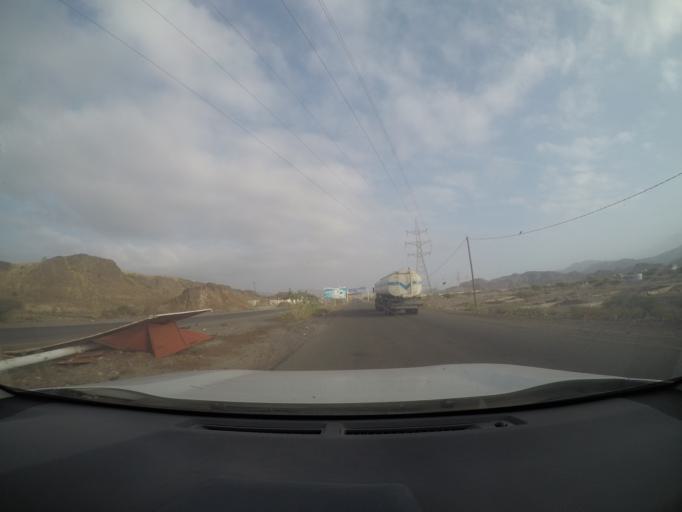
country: YE
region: Lahij
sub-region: Al Milah
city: Al Milah
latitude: 13.2819
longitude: 44.7565
